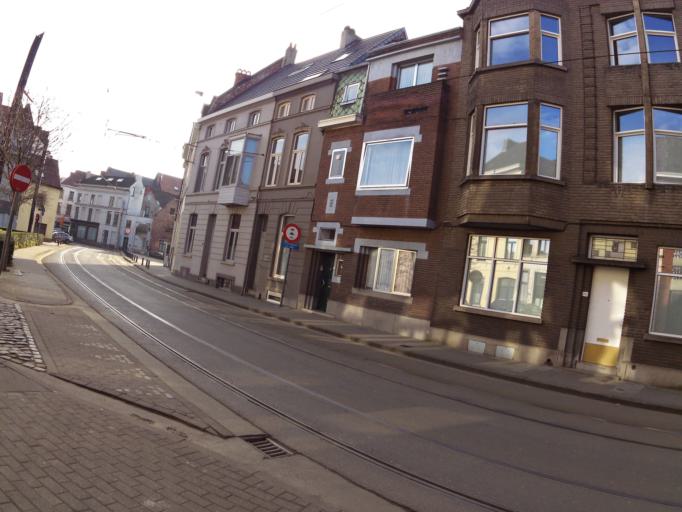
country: BE
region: Flanders
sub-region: Provincie Oost-Vlaanderen
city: Gent
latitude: 51.0571
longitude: 3.7142
